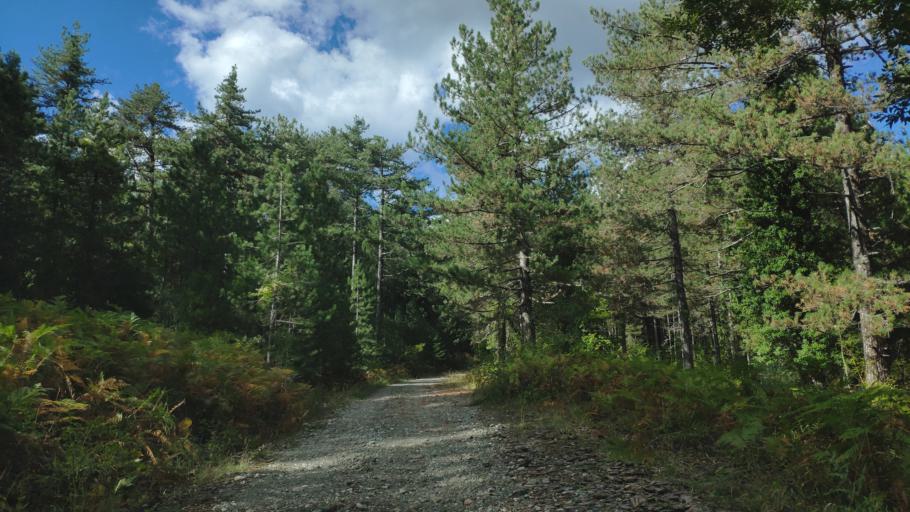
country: GR
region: Epirus
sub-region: Nomos Ioanninon
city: Metsovo
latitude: 39.8897
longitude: 21.2505
